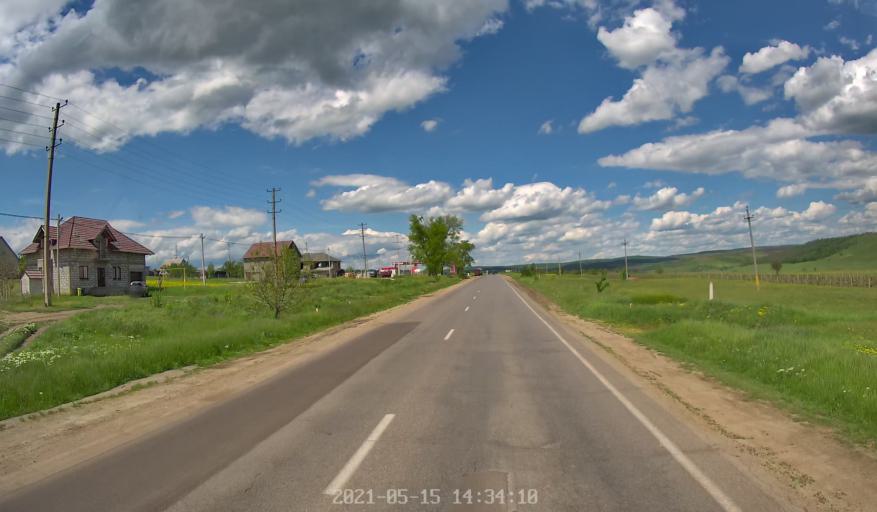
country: MD
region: Hincesti
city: Hincesti
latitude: 46.7505
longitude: 28.5214
